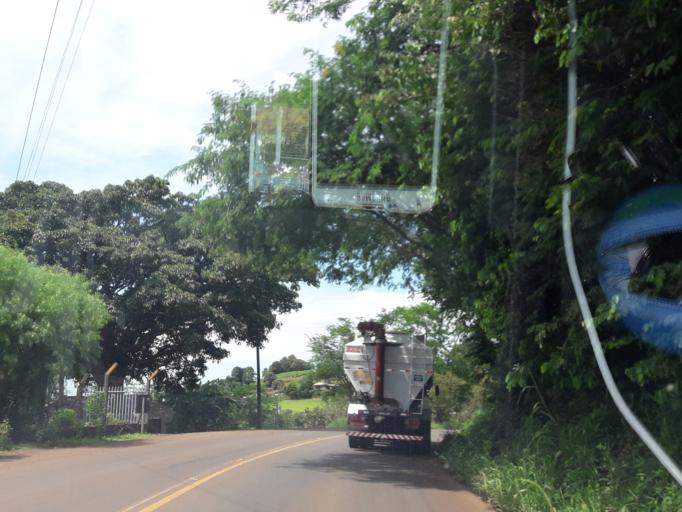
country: BR
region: Rio Grande do Sul
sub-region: Frederico Westphalen
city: Frederico Westphalen
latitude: -26.8593
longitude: -53.4958
